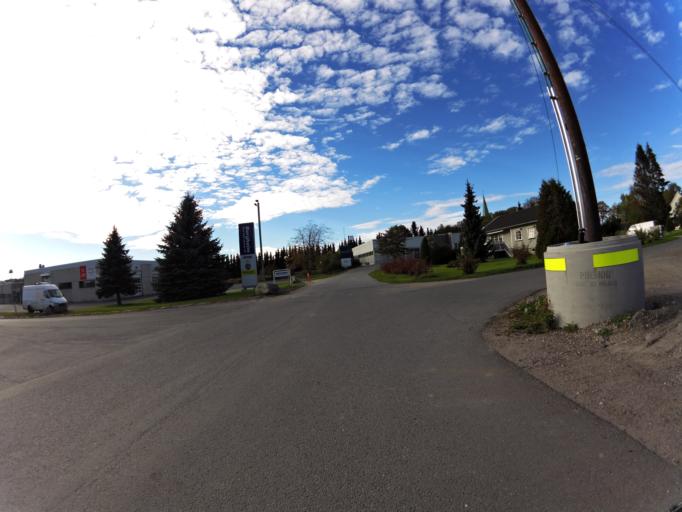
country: NO
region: Ostfold
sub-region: Sarpsborg
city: Sarpsborg
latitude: 59.2905
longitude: 11.0873
